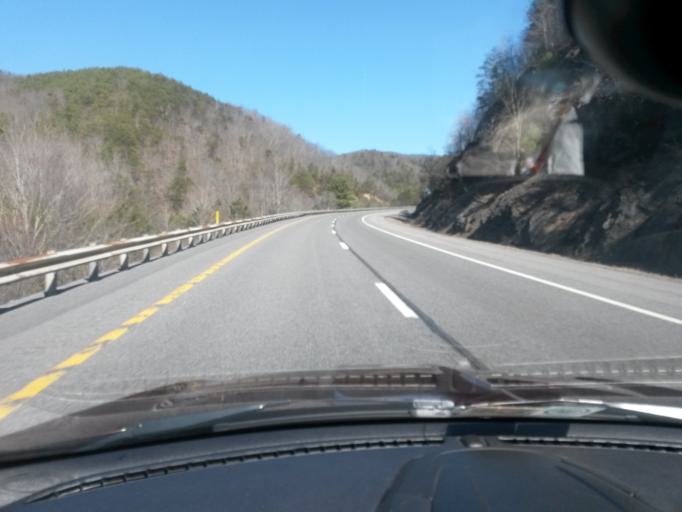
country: US
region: West Virginia
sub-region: Greenbrier County
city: White Sulphur Springs
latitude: 37.7881
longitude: -80.2539
